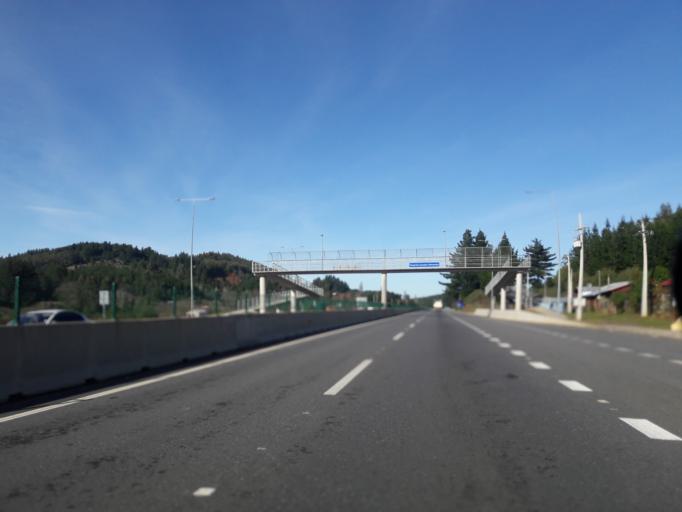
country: CL
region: Biobio
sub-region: Provincia de Biobio
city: Yumbel
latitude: -36.9502
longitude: -72.7495
